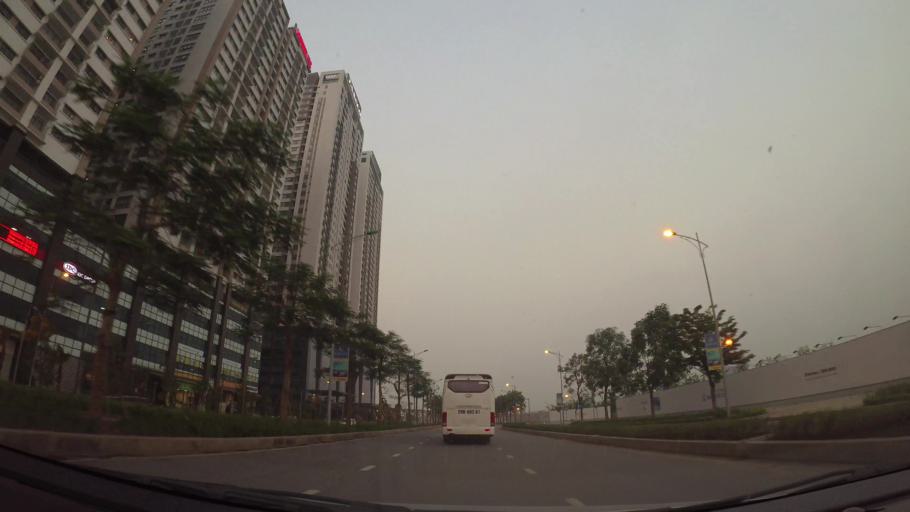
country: VN
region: Ha Noi
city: Tay Ho
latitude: 21.0625
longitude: 105.7944
